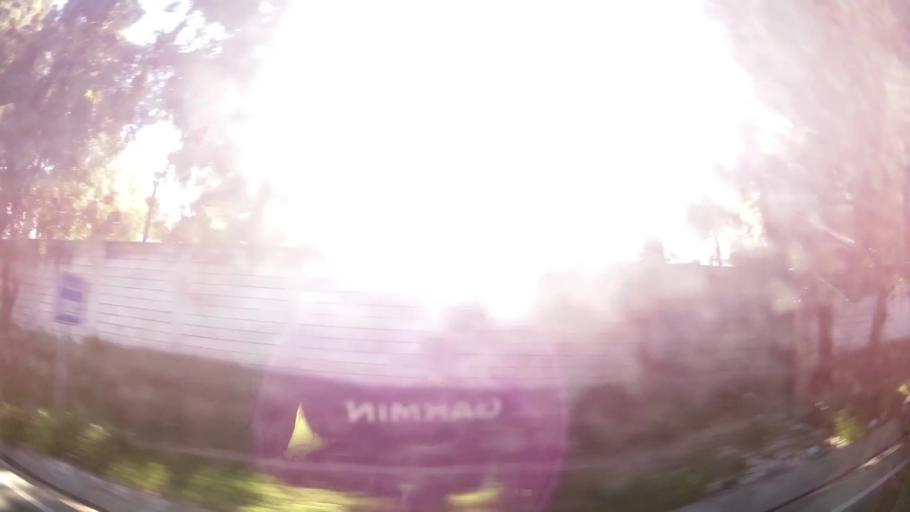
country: GT
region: Guatemala
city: Villa Nueva
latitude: 14.5371
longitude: -90.6053
